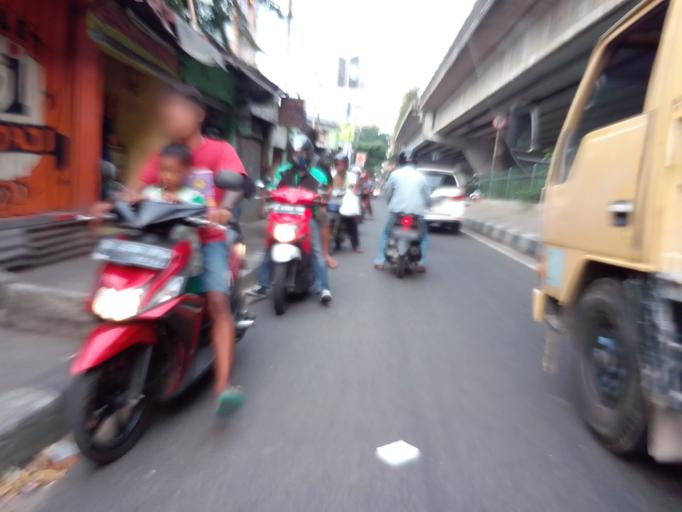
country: ID
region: Jakarta Raya
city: Jakarta
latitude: -6.1659
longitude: 106.8007
